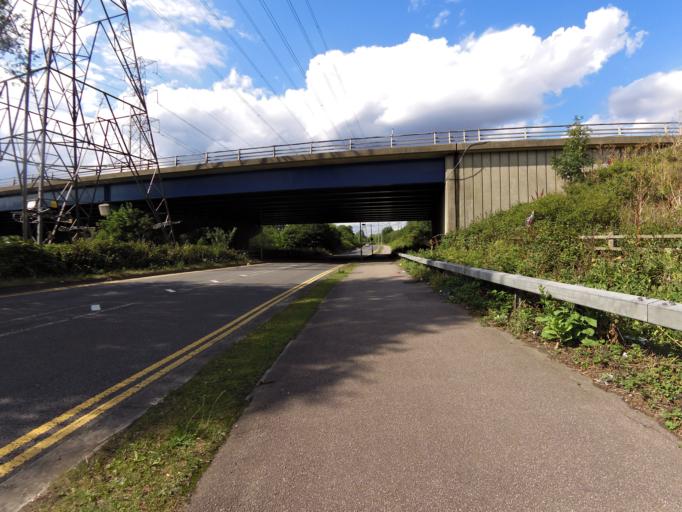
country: GB
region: England
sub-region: Essex
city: Waltham Abbey
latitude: 51.6801
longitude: -0.0105
